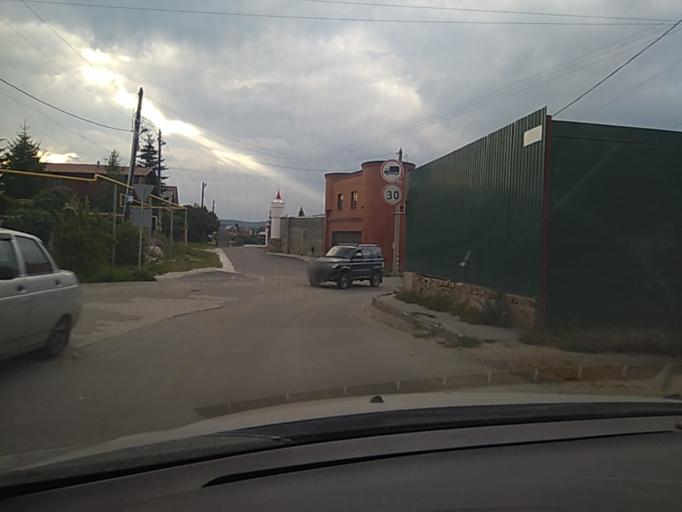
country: RU
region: Chelyabinsk
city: Kyshtym
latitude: 55.7000
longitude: 60.5316
